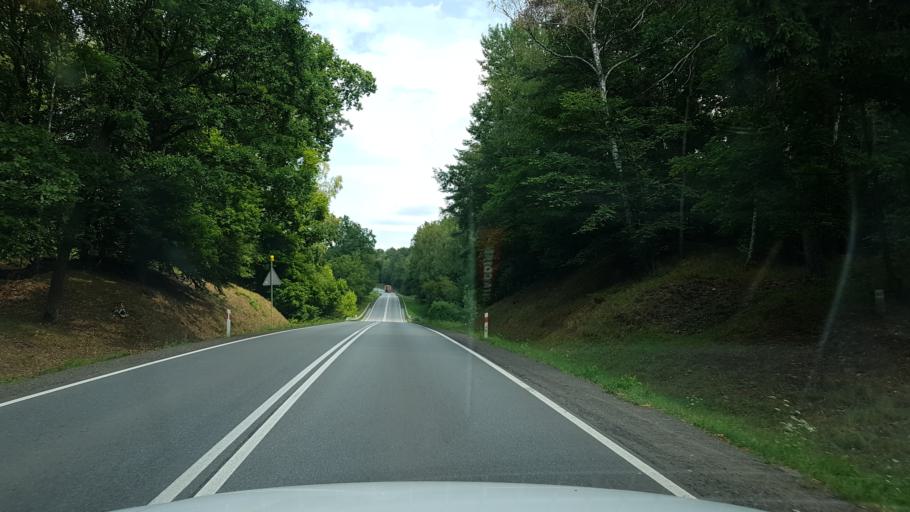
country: PL
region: West Pomeranian Voivodeship
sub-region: Powiat walecki
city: Walcz
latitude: 53.2885
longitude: 16.5144
